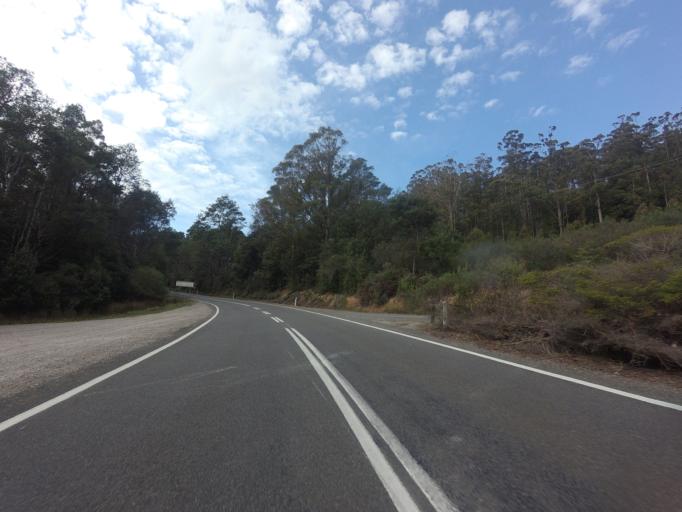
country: AU
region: Tasmania
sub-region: Meander Valley
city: Deloraine
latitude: -41.6470
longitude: 146.7194
